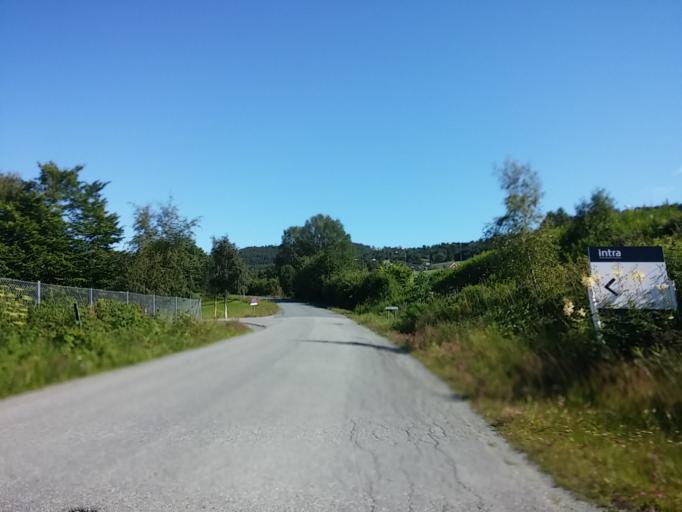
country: NO
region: Sor-Trondelag
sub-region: Malvik
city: Malvik
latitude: 63.4315
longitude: 10.7161
